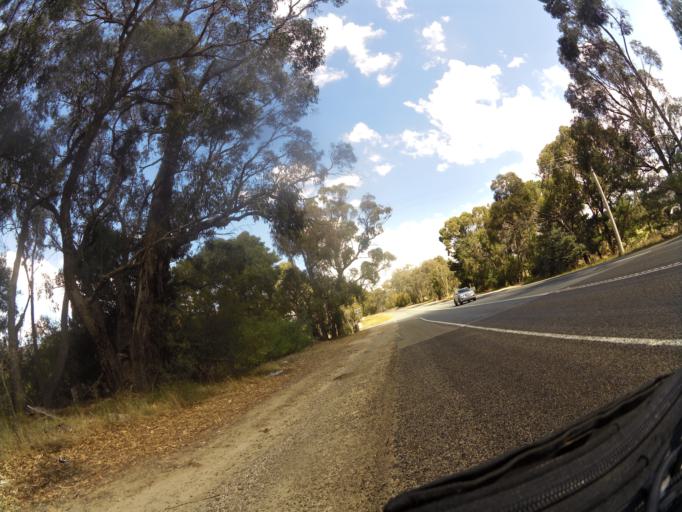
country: AU
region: Victoria
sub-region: Mansfield
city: Mansfield
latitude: -36.8366
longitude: 146.0073
